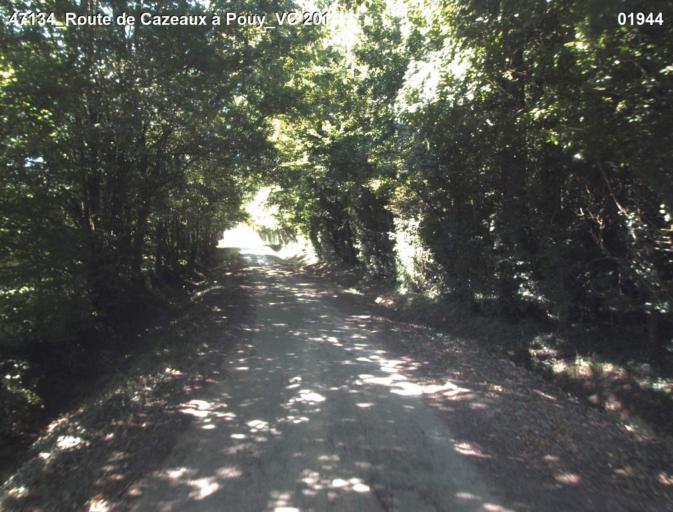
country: FR
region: Aquitaine
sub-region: Departement du Lot-et-Garonne
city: Mezin
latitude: 44.0185
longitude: 0.3120
